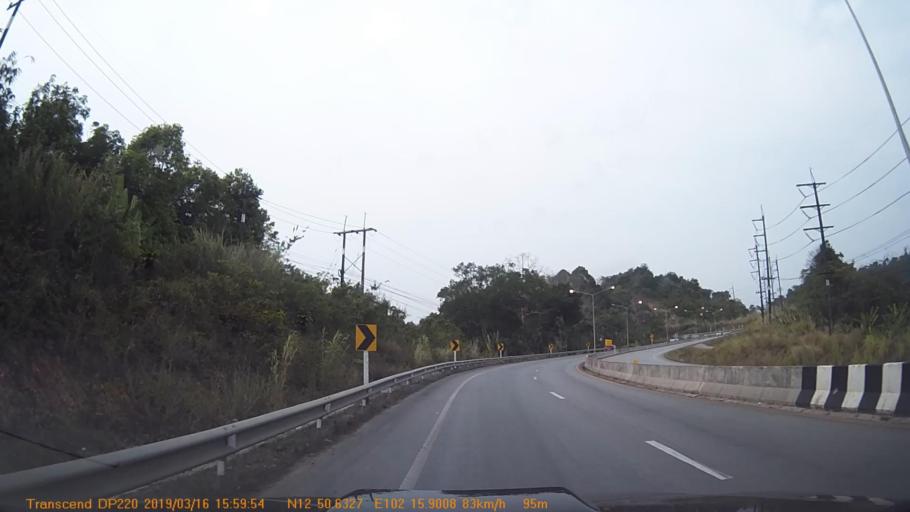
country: TH
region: Chanthaburi
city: Pong Nam Ron
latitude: 12.8443
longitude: 102.2650
